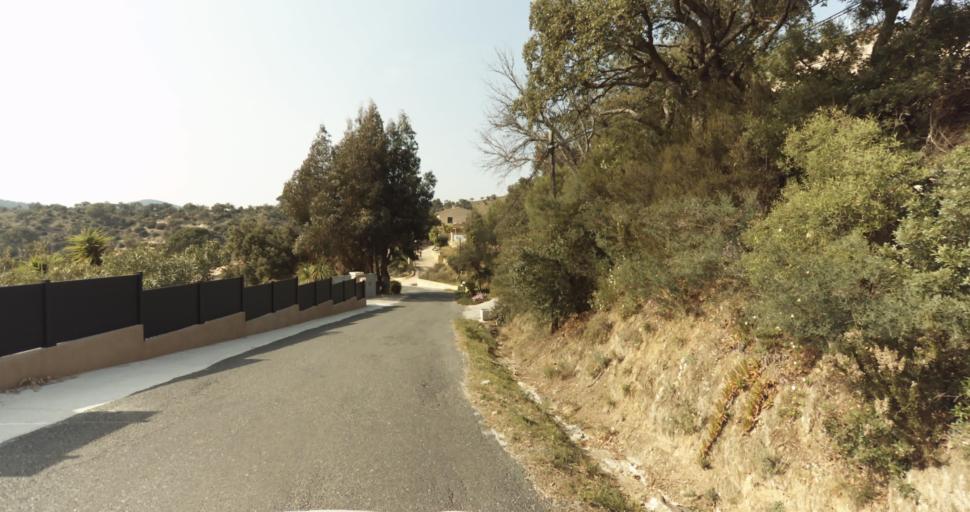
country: FR
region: Provence-Alpes-Cote d'Azur
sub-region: Departement du Var
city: Bormes-les-Mimosas
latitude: 43.1486
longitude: 6.3276
